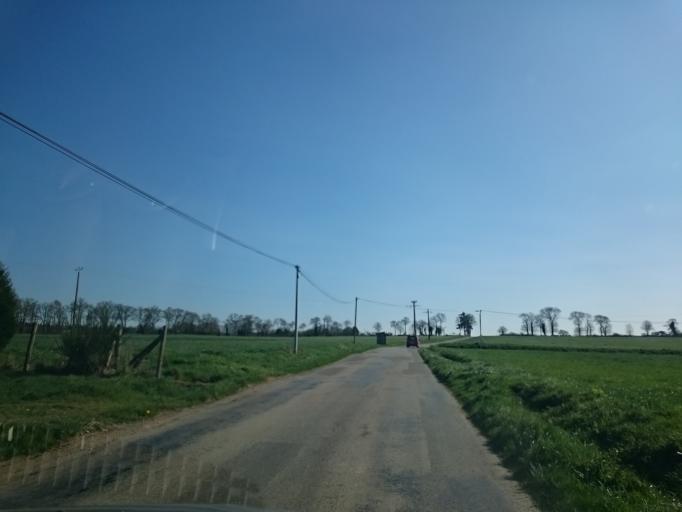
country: FR
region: Brittany
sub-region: Departement d'Ille-et-Vilaine
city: Orgeres
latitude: 47.9869
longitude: -1.6733
